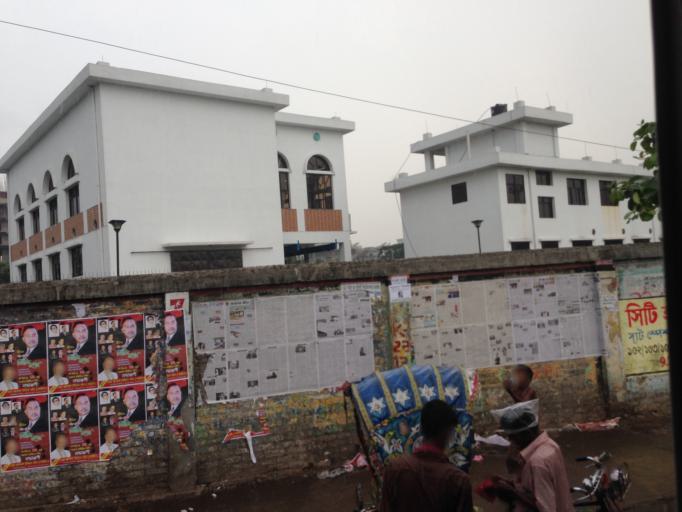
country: BD
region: Dhaka
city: Paltan
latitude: 23.7249
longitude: 90.4287
